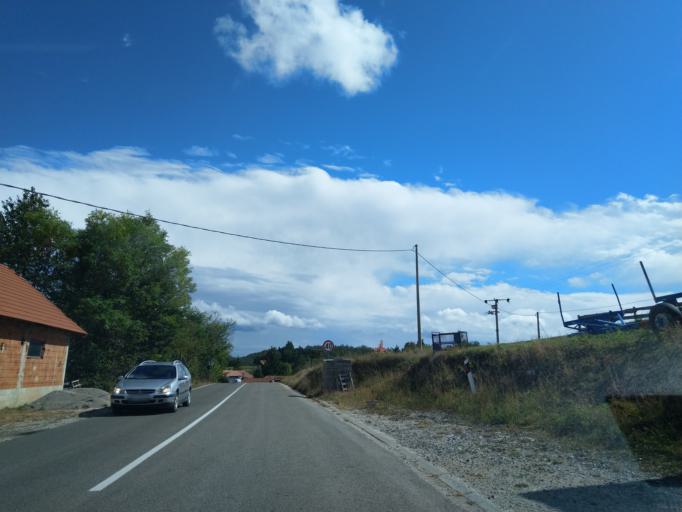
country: RS
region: Central Serbia
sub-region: Zlatiborski Okrug
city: Cajetina
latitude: 43.7211
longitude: 19.8324
